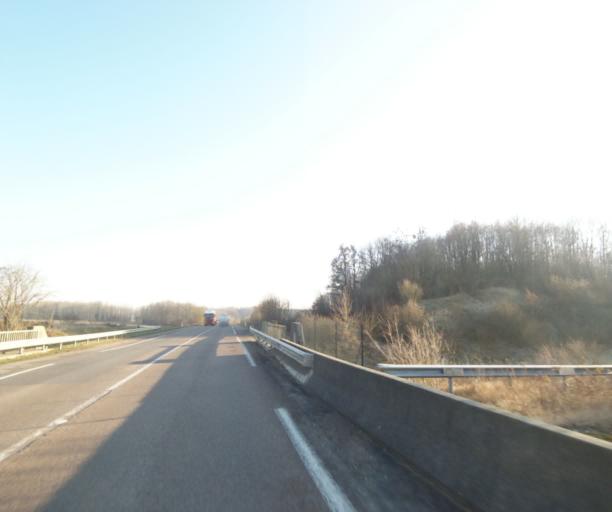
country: FR
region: Champagne-Ardenne
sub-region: Departement de la Haute-Marne
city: Chevillon
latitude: 48.5017
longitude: 5.1050
